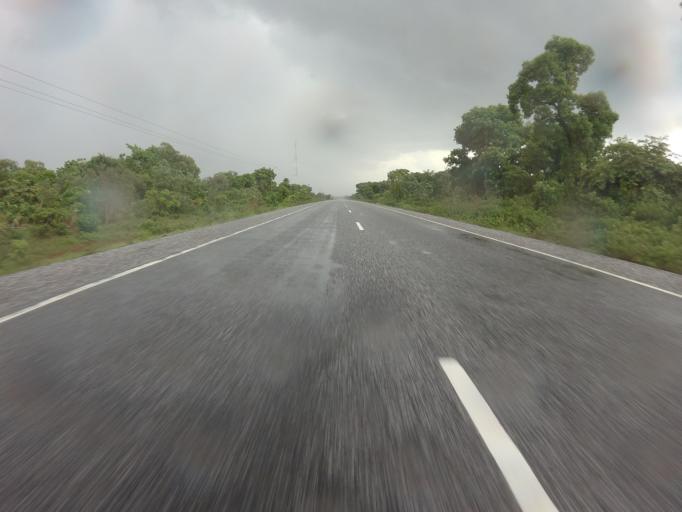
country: GH
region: Northern
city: Tamale
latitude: 9.1367
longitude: -1.5746
